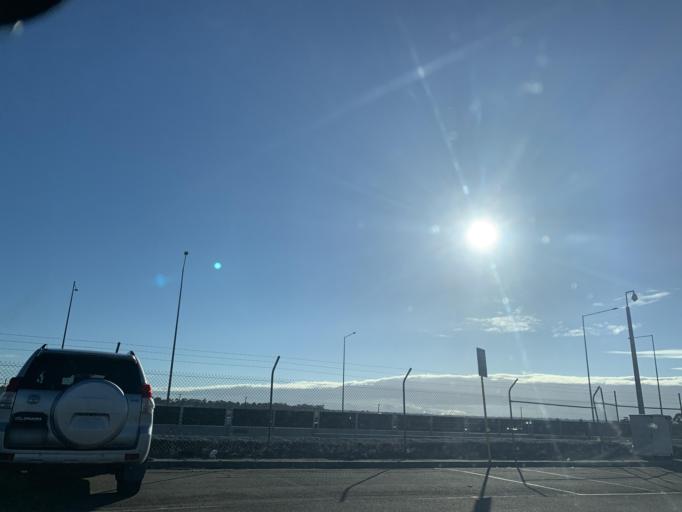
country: AU
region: Victoria
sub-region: Hume
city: Westmeadows
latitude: -37.6785
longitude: 144.8659
